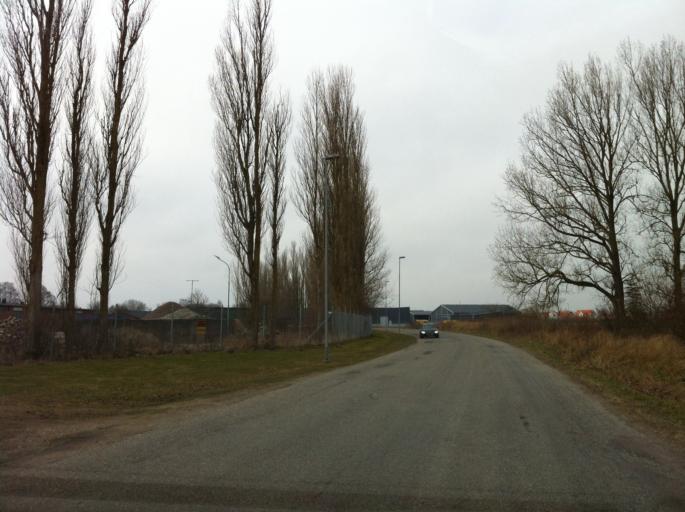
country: SE
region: Skane
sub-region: Kavlinge Kommun
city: Kaevlinge
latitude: 55.7711
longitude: 13.1340
